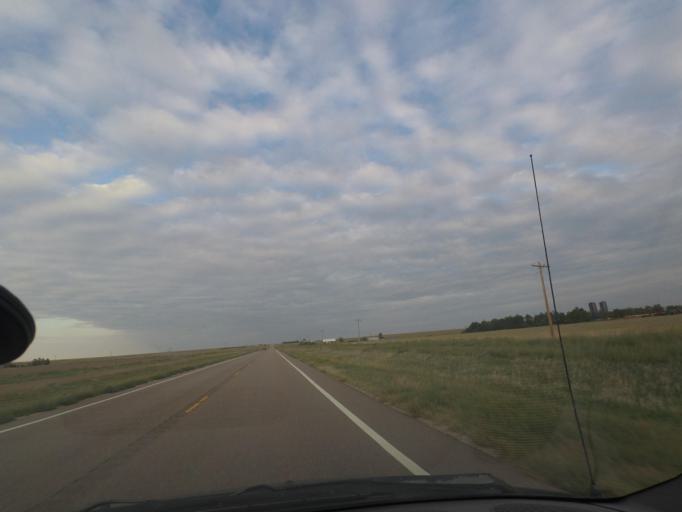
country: US
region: Kansas
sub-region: Cheyenne County
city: Saint Francis
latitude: 39.7567
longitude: -102.0353
